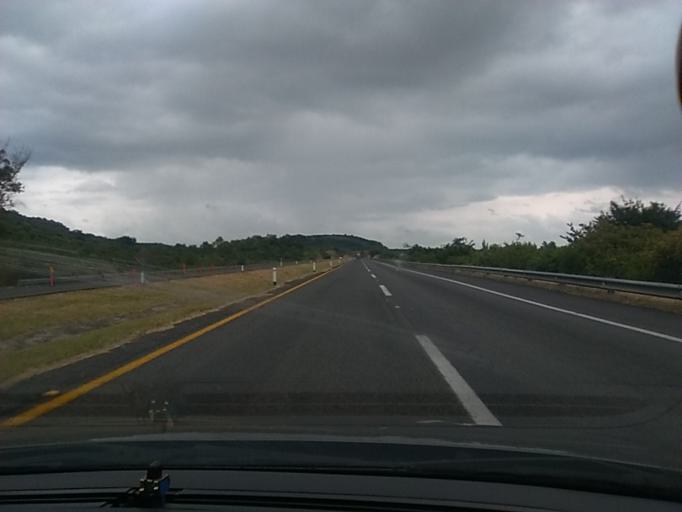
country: MX
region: Jalisco
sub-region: Zapotlan del Rey
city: Zapotlan del Rey
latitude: 20.4843
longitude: -102.9397
